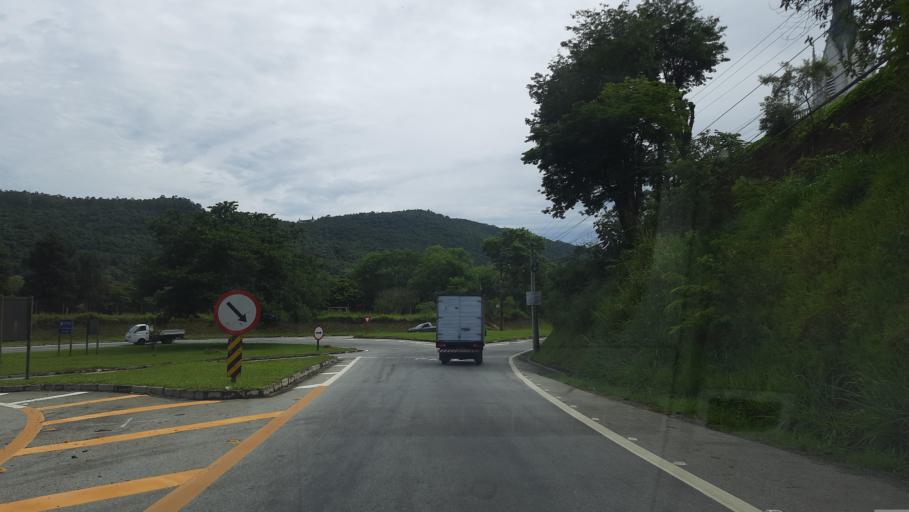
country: BR
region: Sao Paulo
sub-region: Franco Da Rocha
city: Franco da Rocha
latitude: -23.3385
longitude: -46.6599
